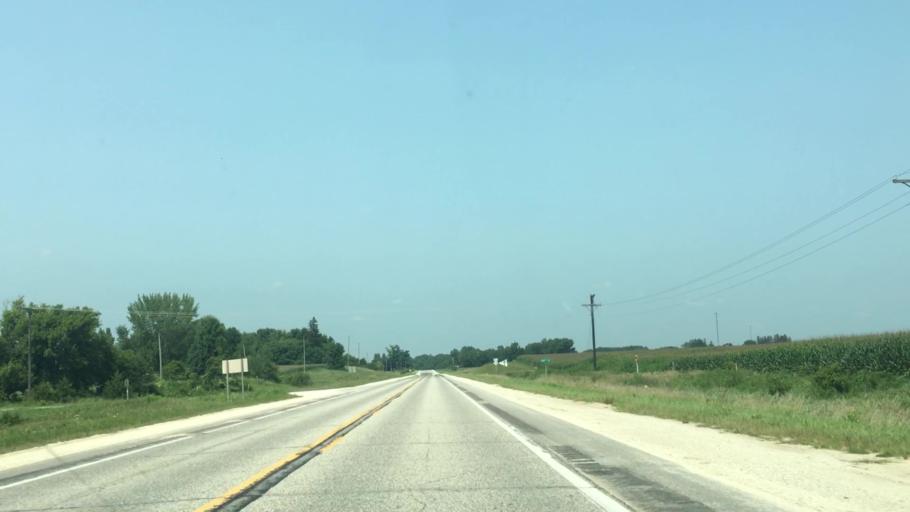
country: US
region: Iowa
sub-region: Fayette County
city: Fayette
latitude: 42.8186
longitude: -91.8051
